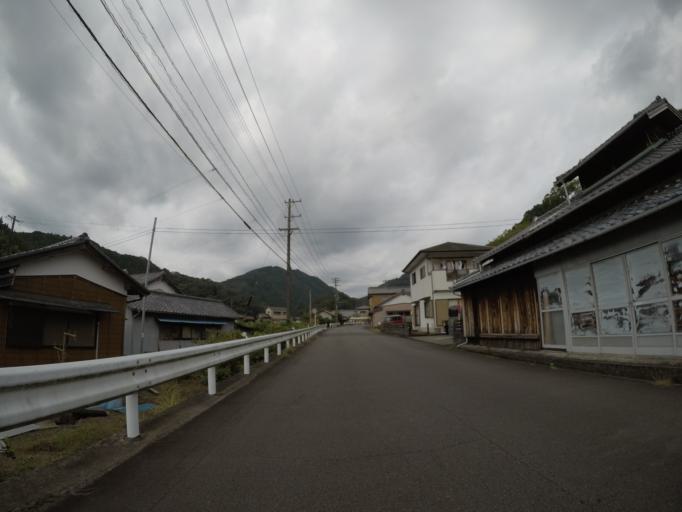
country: JP
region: Shizuoka
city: Fujieda
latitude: 34.9105
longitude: 138.1939
